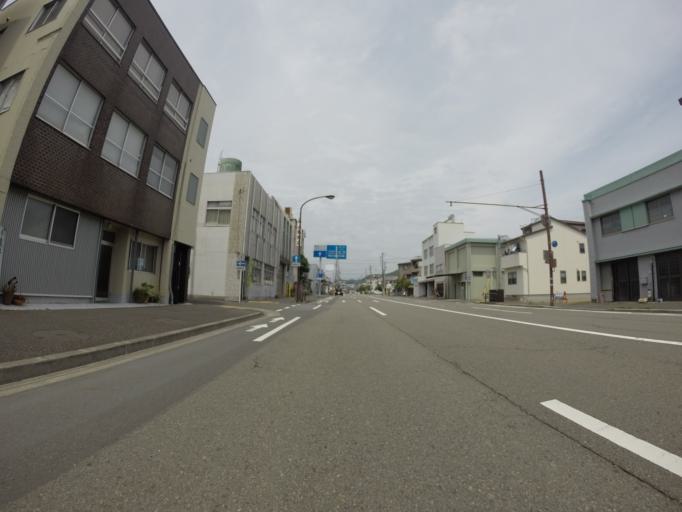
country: JP
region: Shizuoka
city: Shizuoka-shi
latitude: 34.9768
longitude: 138.3697
